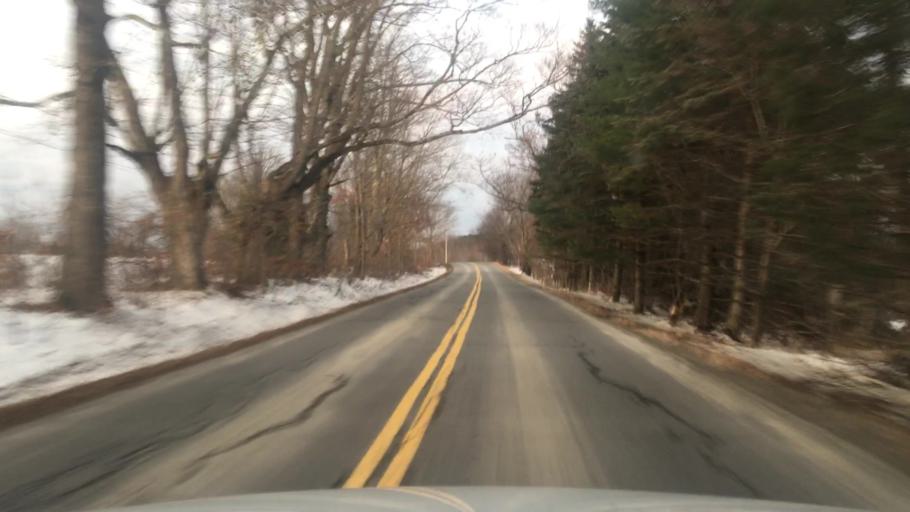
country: US
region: Maine
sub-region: Somerset County
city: Canaan
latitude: 44.7525
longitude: -69.6292
